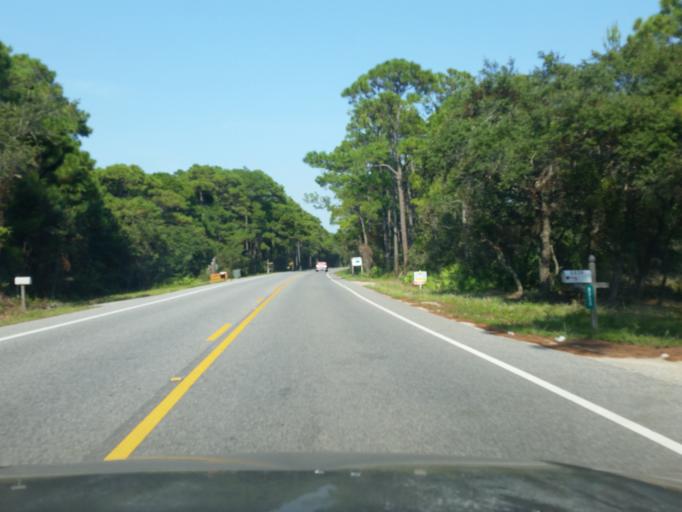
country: US
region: Alabama
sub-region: Baldwin County
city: Gulf Shores
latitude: 30.2383
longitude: -87.8713
